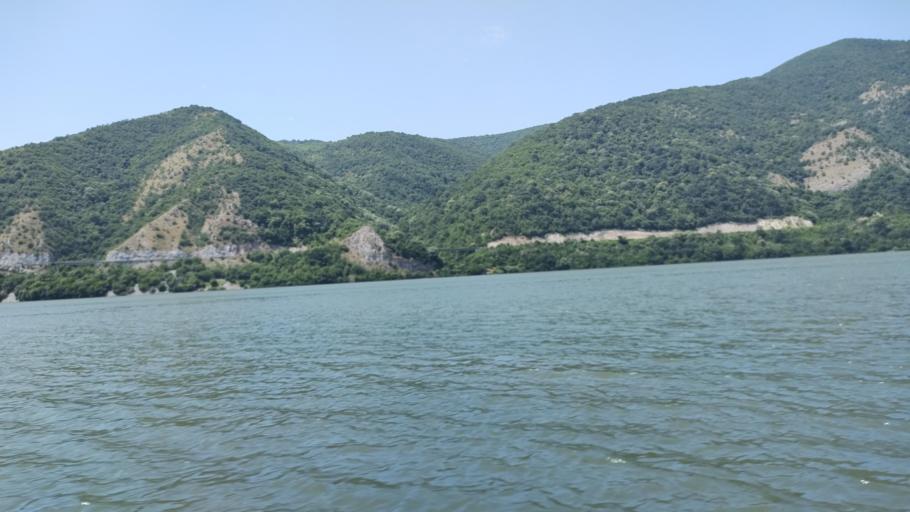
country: RO
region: Caras-Severin
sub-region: Comuna Berzasca
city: Berzasca
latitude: 44.5729
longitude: 22.0293
